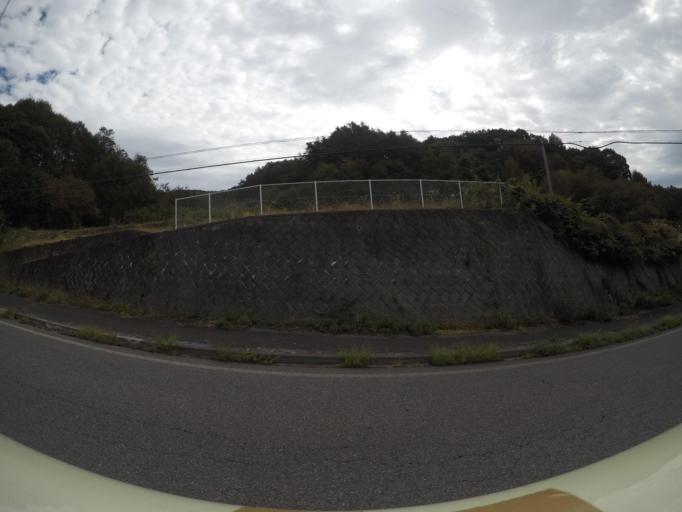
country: JP
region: Nagano
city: Chino
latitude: 35.9379
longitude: 138.1000
